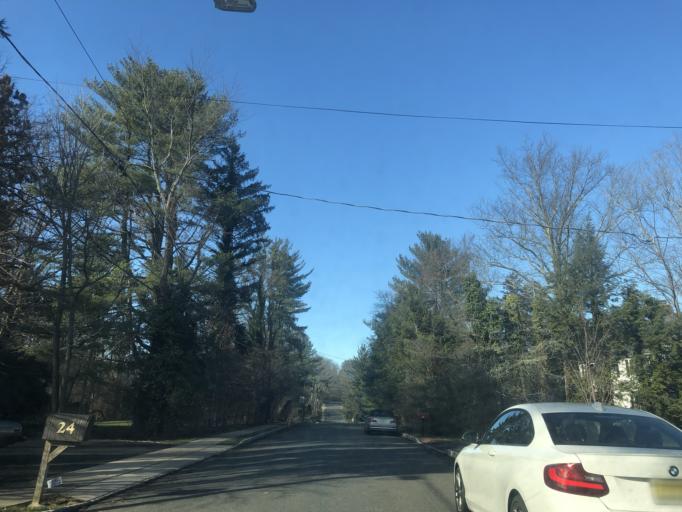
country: US
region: New Jersey
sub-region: Somerset County
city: Kingston
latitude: 40.3610
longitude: -74.6328
